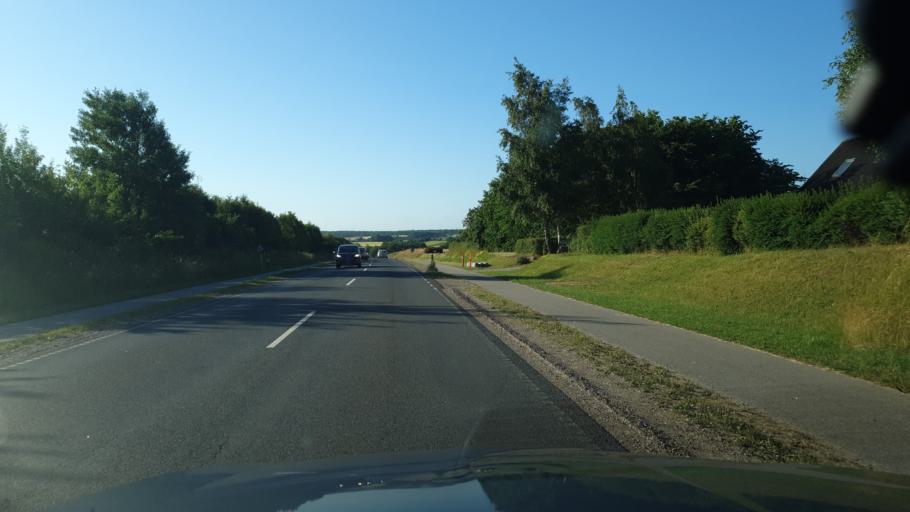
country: DK
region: Zealand
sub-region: Soro Kommune
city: Frederiksberg
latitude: 55.3931
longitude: 11.6397
